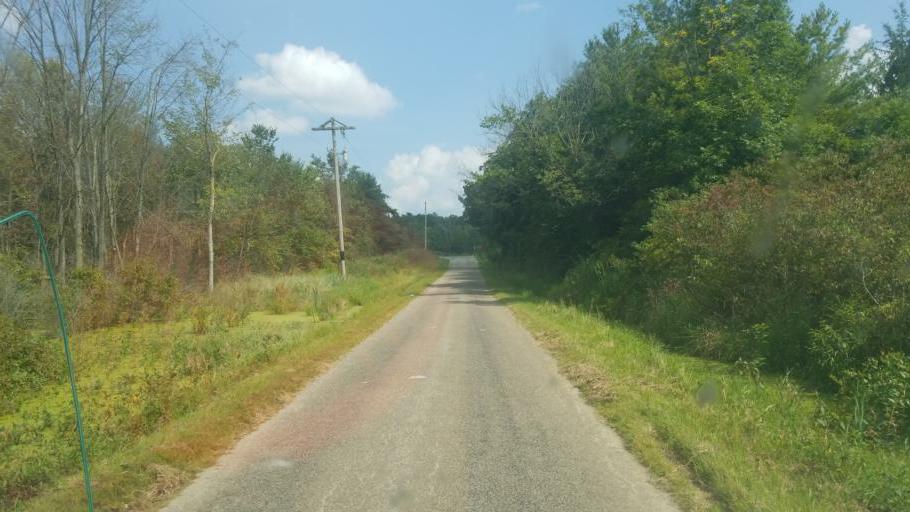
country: US
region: Ohio
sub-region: Huron County
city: New London
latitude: 41.0111
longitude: -82.4082
